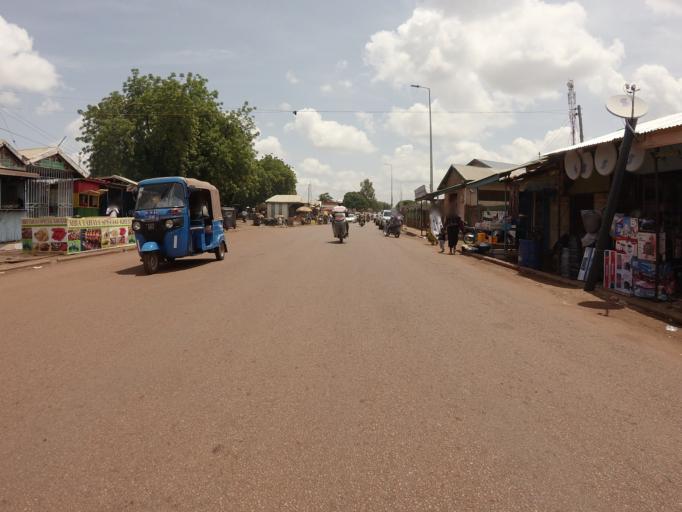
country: GH
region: Northern
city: Tamale
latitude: 9.4012
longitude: -0.8462
